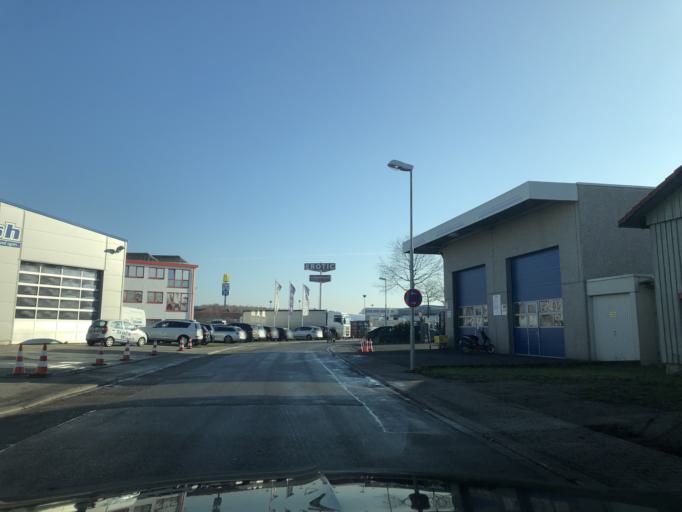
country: DE
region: Baden-Wuerttemberg
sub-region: Karlsruhe Region
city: Karlsdorf-Neuthard
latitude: 49.1488
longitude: 8.5508
